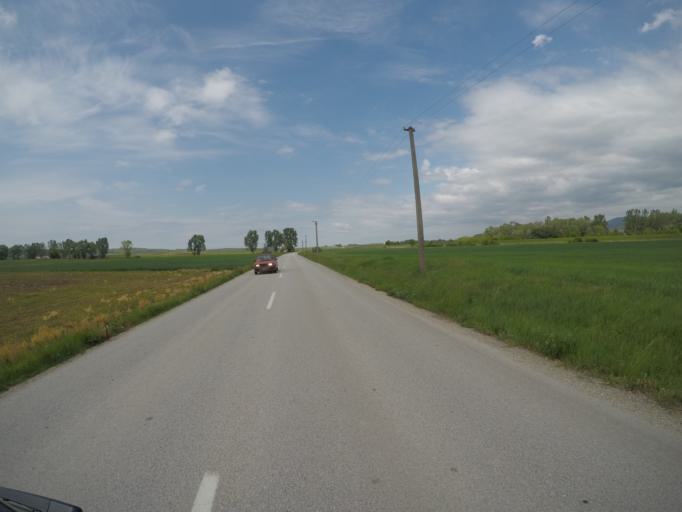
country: HU
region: Komarom-Esztergom
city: Esztergom
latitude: 47.8952
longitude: 18.7545
